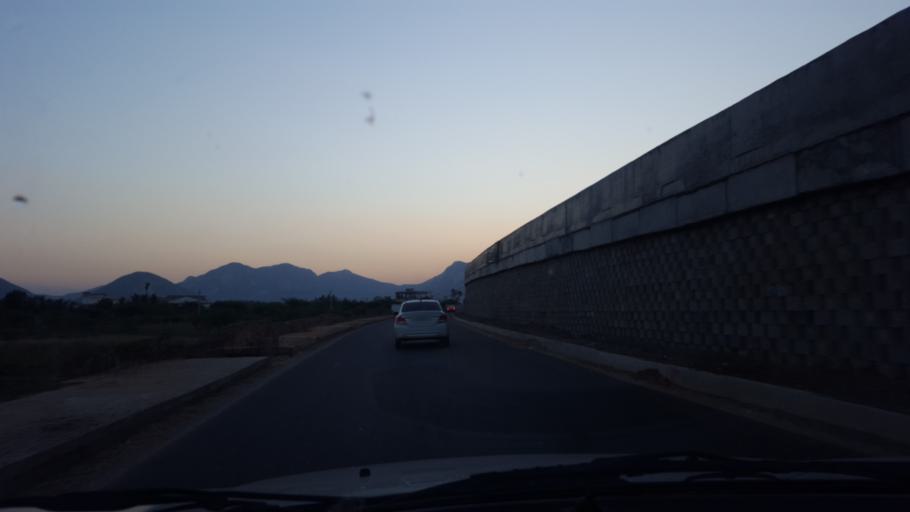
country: IN
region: Andhra Pradesh
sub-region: Chittoor
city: Narasingapuram
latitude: 13.5884
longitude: 79.3433
